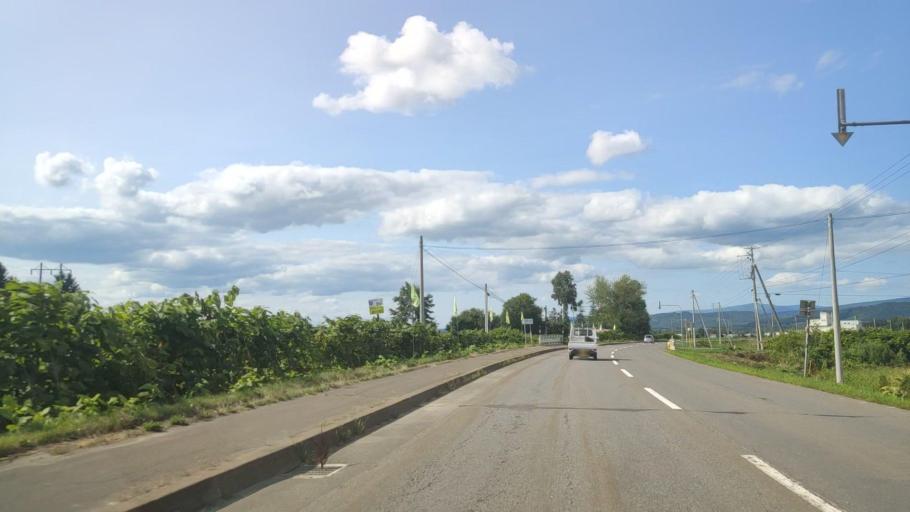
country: JP
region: Hokkaido
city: Nayoro
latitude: 44.4267
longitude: 142.3999
